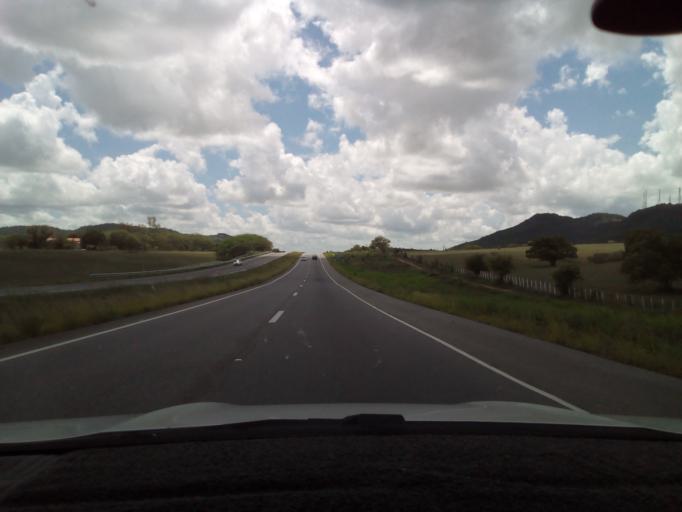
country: BR
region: Paraiba
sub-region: Gurinhem
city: Gurinhem
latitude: -7.1817
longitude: -35.4331
